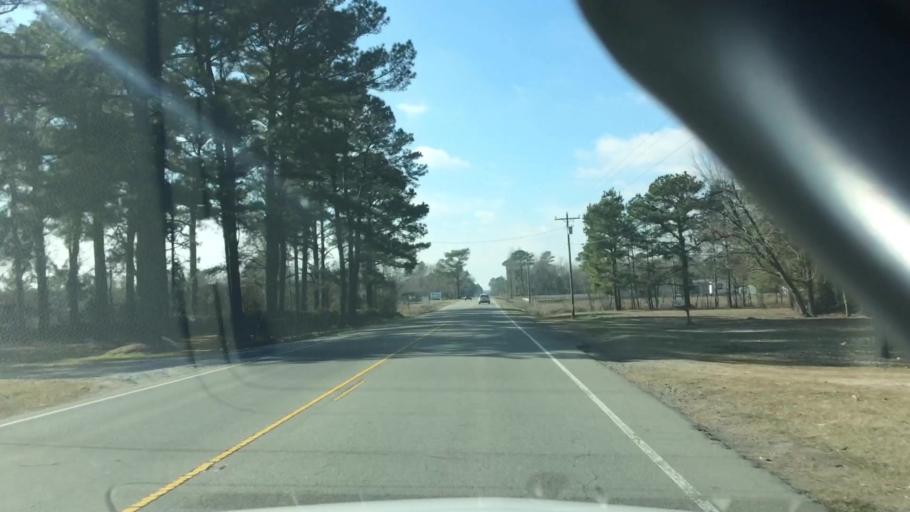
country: US
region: North Carolina
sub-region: Duplin County
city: Wallace
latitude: 34.7923
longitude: -77.8692
